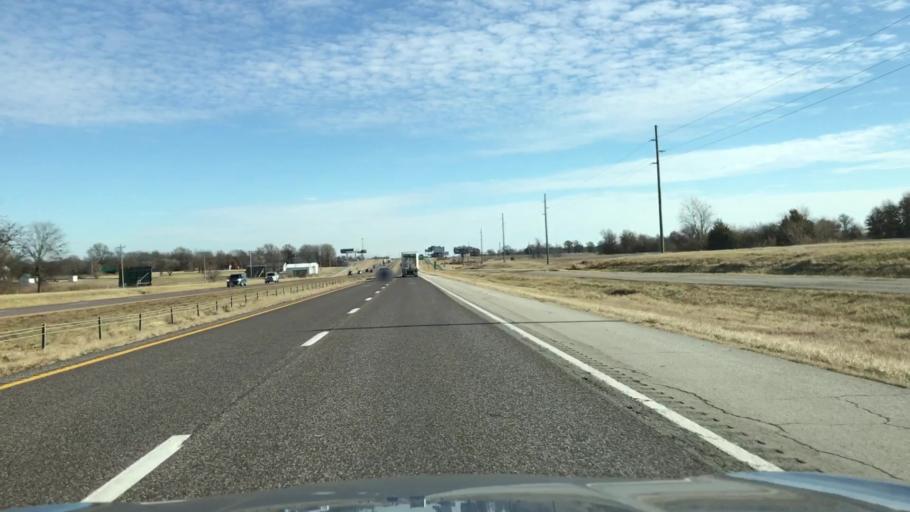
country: US
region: Missouri
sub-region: Callaway County
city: Fulton
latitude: 38.9520
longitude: -92.0386
